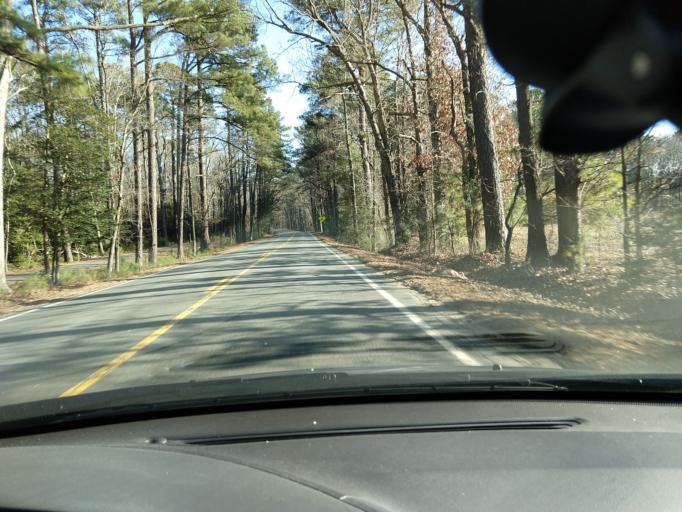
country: US
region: Virginia
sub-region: Surry County
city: Surry
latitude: 37.2644
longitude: -76.8927
